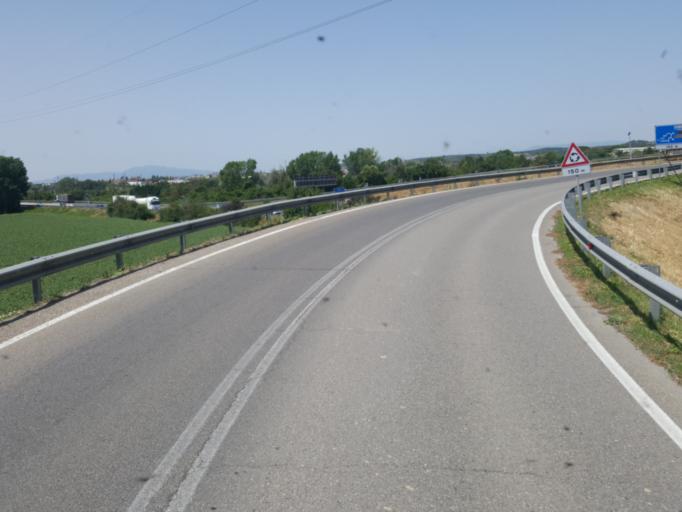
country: IT
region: Tuscany
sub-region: Province of Florence
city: Limite
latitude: 43.7177
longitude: 10.9828
